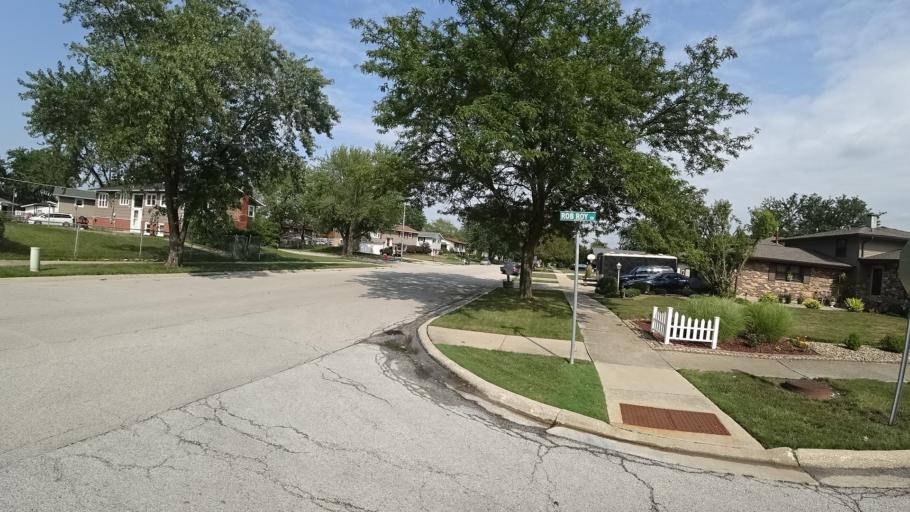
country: US
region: Illinois
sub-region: Cook County
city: Oak Forest
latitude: 41.6099
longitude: -87.7717
